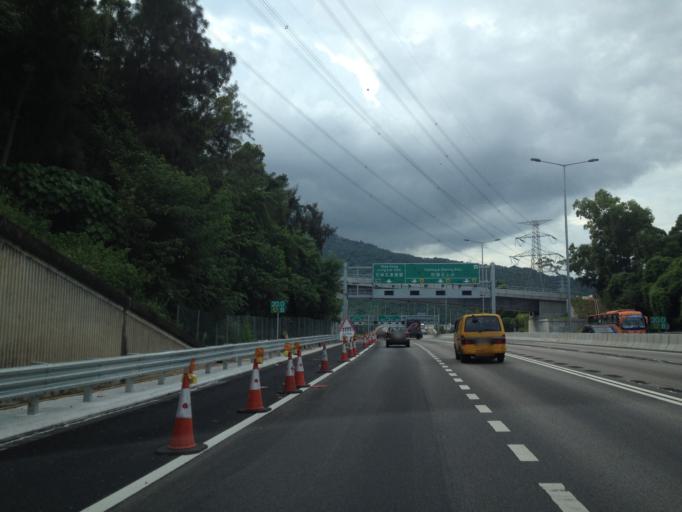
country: HK
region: Tai Po
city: Tai Po
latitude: 22.4556
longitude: 114.1502
